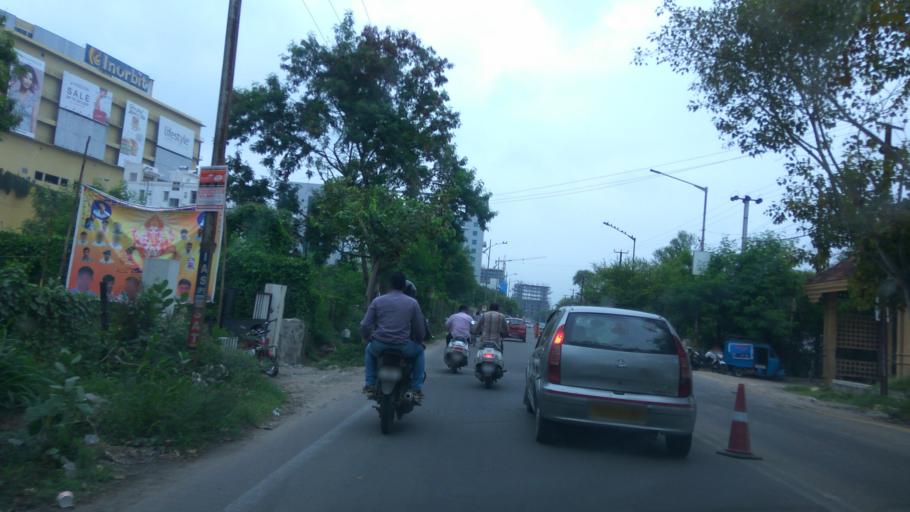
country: IN
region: Telangana
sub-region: Rangareddi
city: Kukatpalli
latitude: 17.4333
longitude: 78.3881
